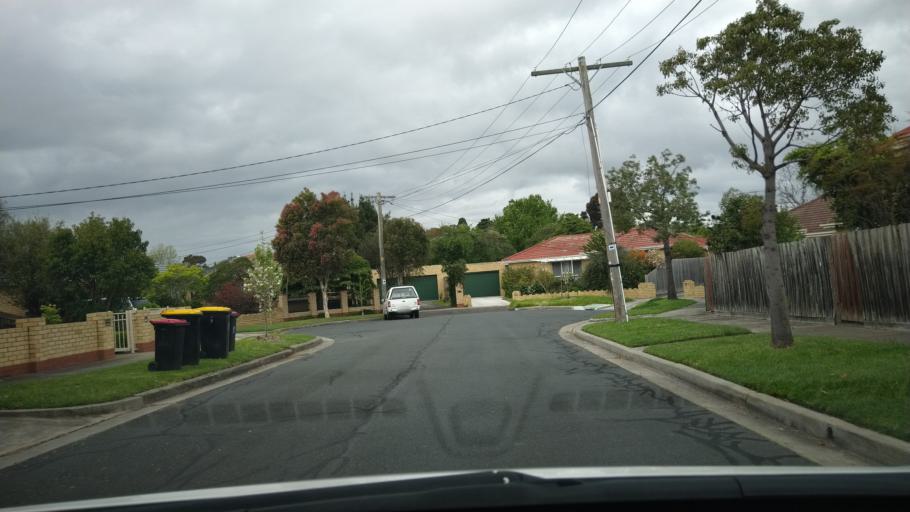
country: AU
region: Victoria
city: Highett
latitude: -37.9551
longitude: 145.0646
